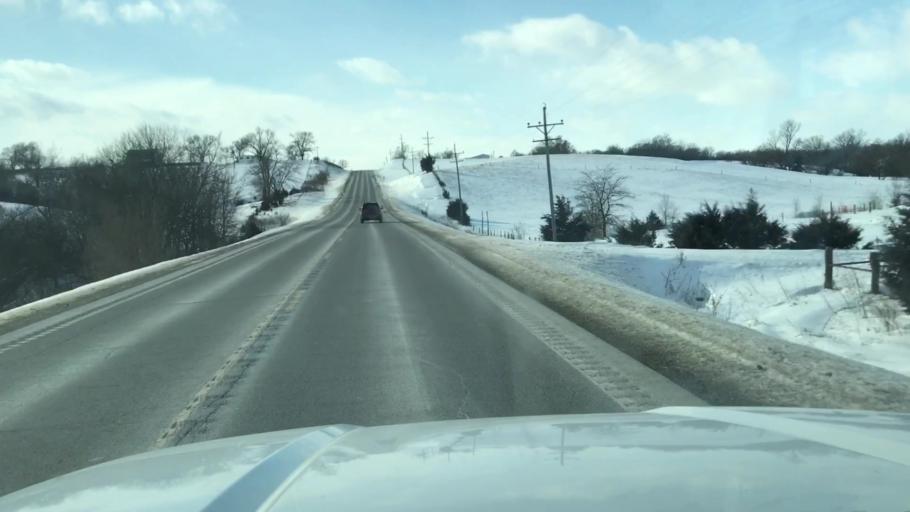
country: US
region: Missouri
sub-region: Nodaway County
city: Maryville
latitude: 40.3435
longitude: -94.6985
